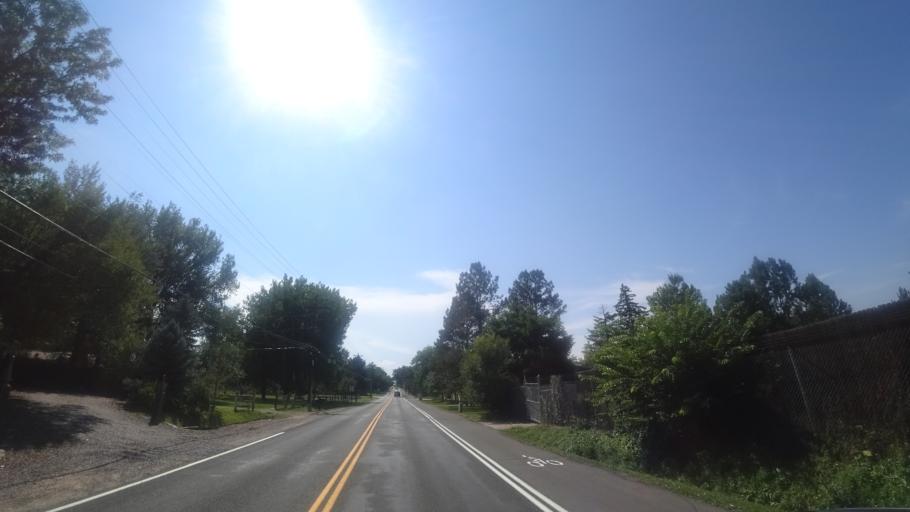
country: US
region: Colorado
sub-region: Arapahoe County
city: Cherry Hills Village
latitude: 39.6387
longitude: -104.9674
